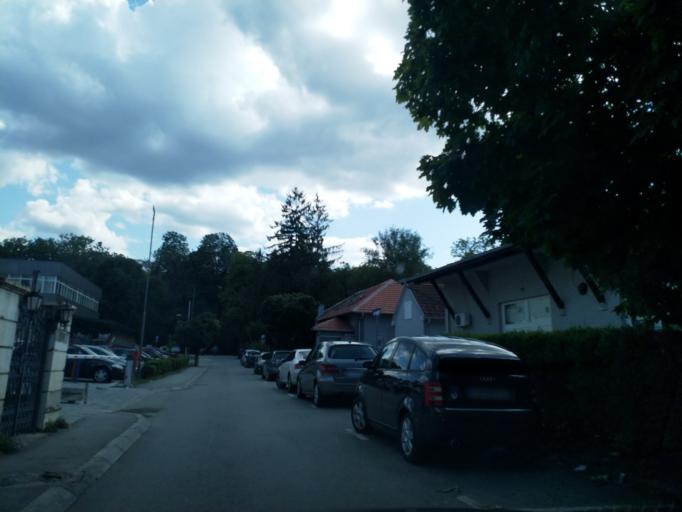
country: RS
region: Central Serbia
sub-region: Raski Okrug
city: Vrnjacka Banja
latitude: 43.6215
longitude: 20.8952
